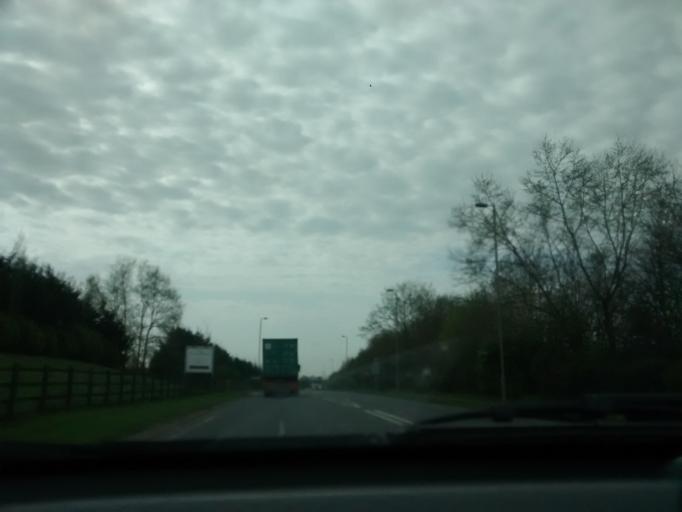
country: GB
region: England
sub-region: Oxfordshire
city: Bicester
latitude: 51.9014
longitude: -1.1274
